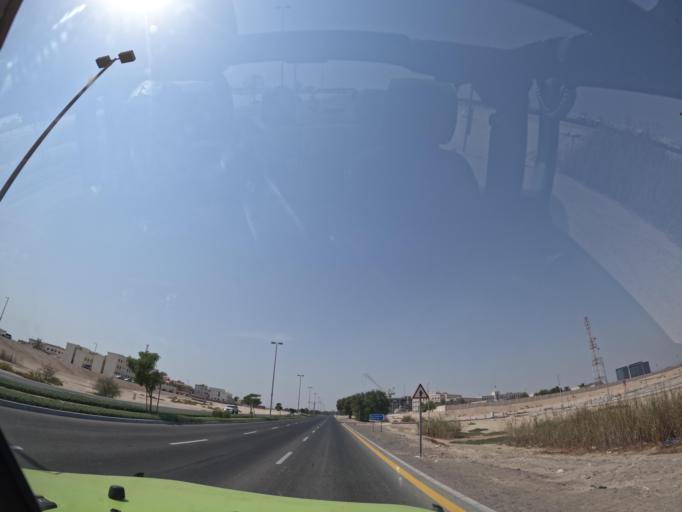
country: AE
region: Abu Dhabi
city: Abu Dhabi
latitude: 24.3120
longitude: 54.6124
